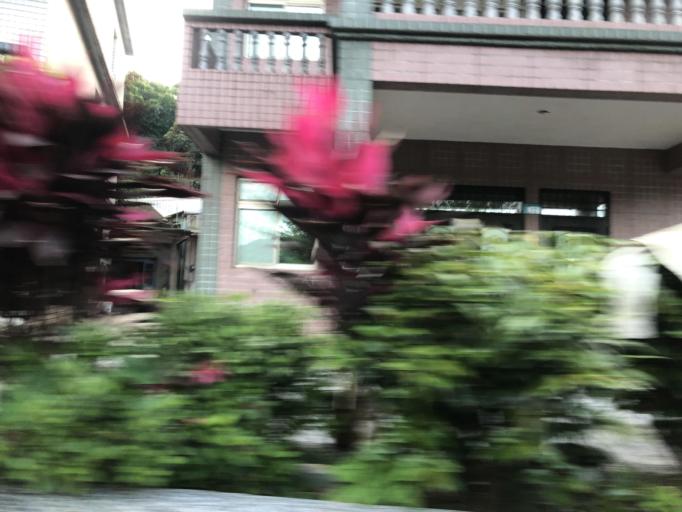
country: TW
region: Taiwan
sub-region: Keelung
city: Keelung
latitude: 25.1991
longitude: 121.6466
